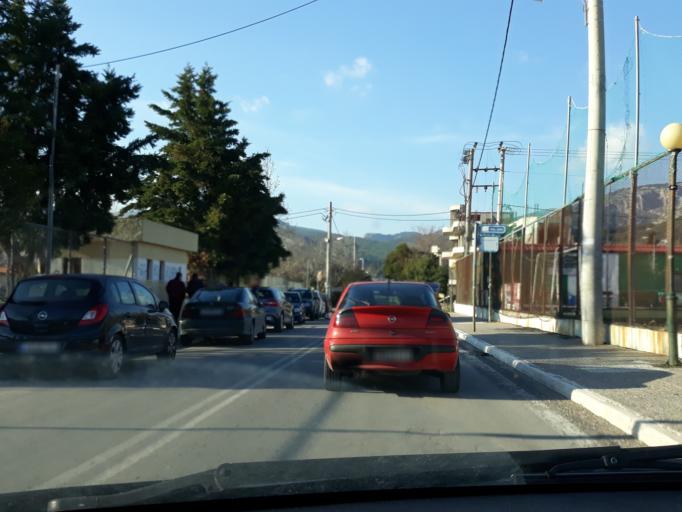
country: GR
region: Attica
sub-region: Nomarchia Dytikis Attikis
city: Fyli
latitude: 38.1069
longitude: 23.6675
